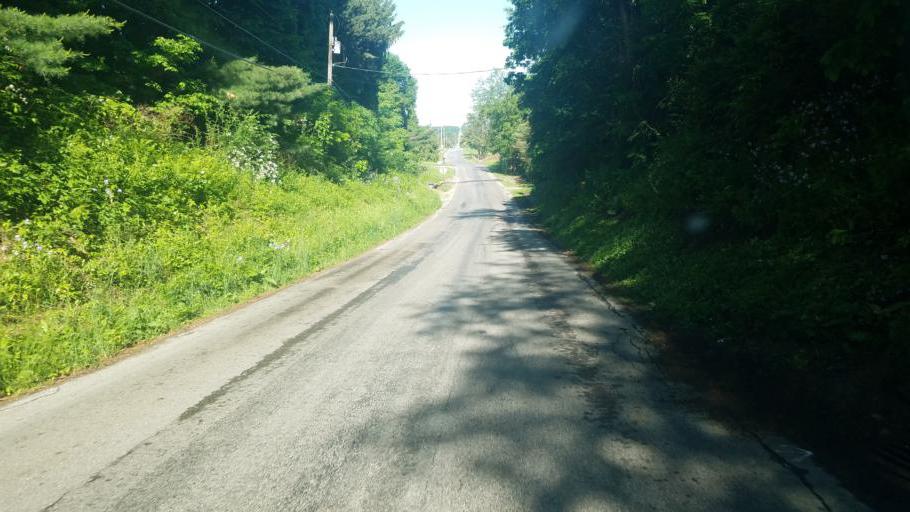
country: US
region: Ohio
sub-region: Sandusky County
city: Bellville
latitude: 40.5864
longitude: -82.5694
